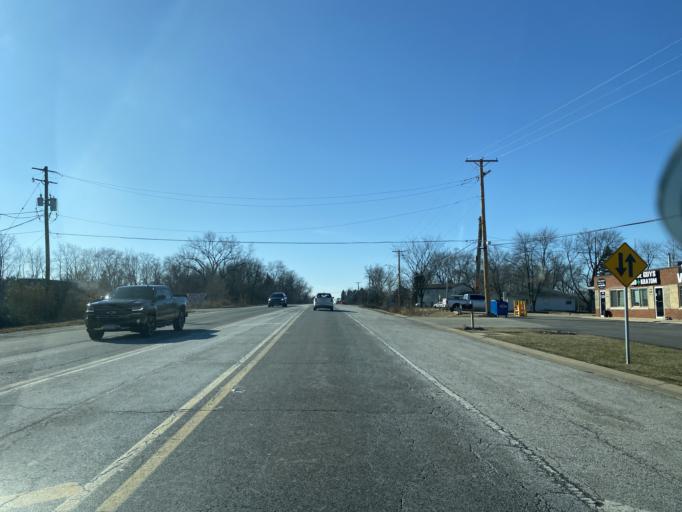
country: US
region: Illinois
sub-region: Will County
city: Lockport
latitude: 41.6253
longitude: -88.0241
